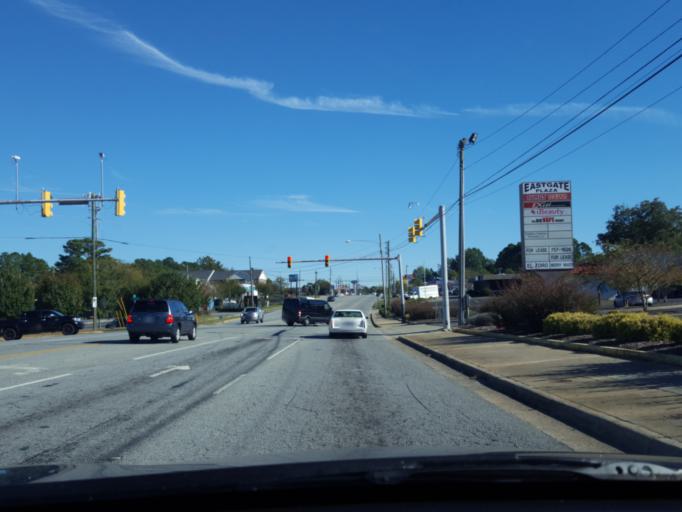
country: US
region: North Carolina
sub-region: Pitt County
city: Greenville
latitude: 35.6030
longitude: -77.3405
